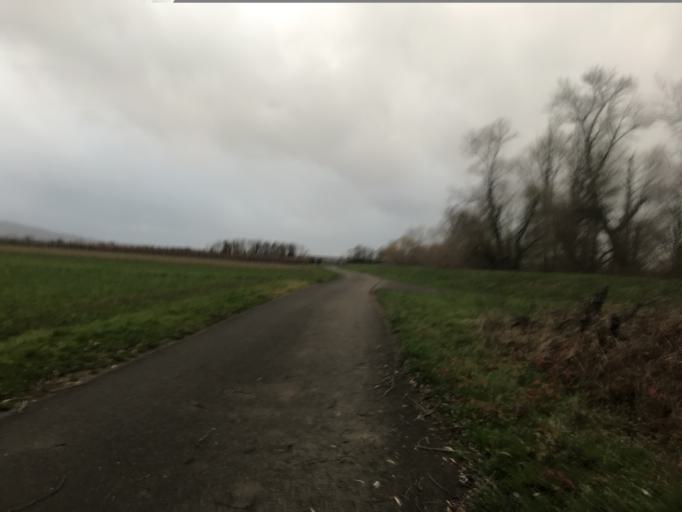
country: DE
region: Rheinland-Pfalz
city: Oestrich-Winkel
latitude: 49.9818
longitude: 8.0076
